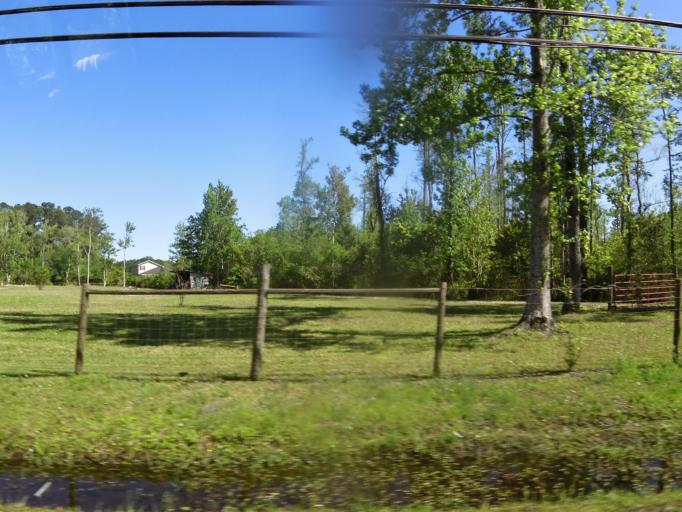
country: US
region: Florida
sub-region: Duval County
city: Jacksonville
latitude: 30.4628
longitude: -81.5908
